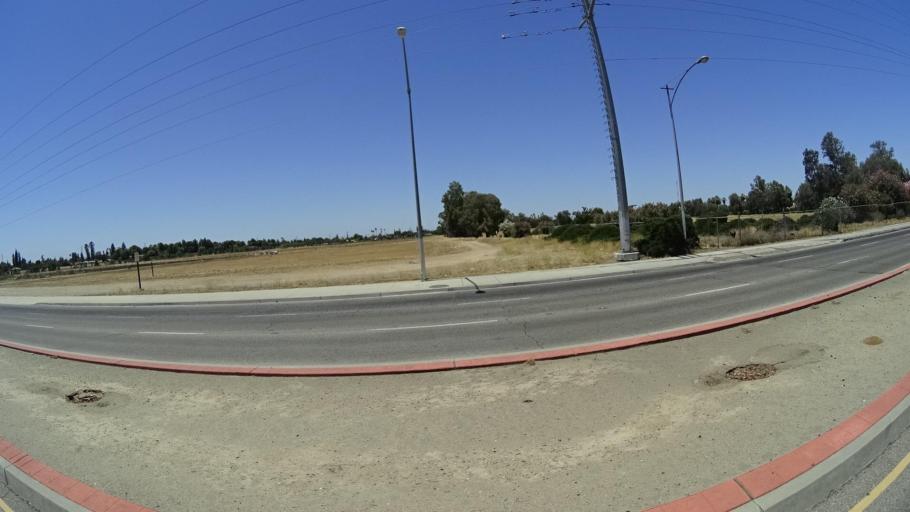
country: US
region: California
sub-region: Fresno County
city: Sunnyside
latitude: 36.7553
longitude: -119.7003
